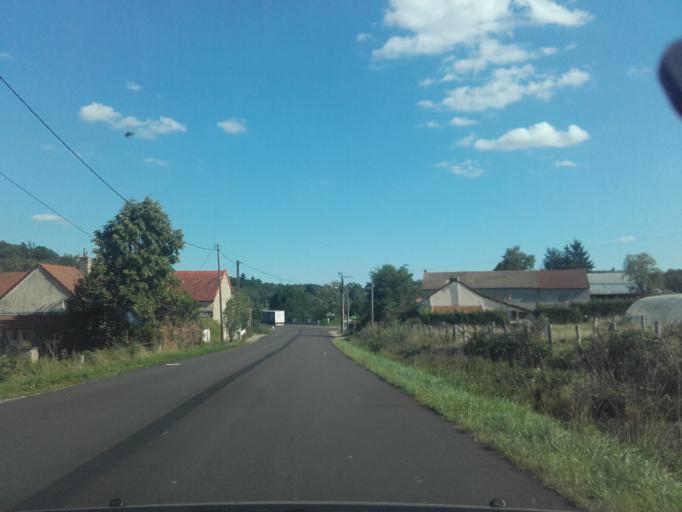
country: FR
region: Bourgogne
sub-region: Departement de Saone-et-Loire
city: Epinac
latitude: 46.9707
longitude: 4.5280
